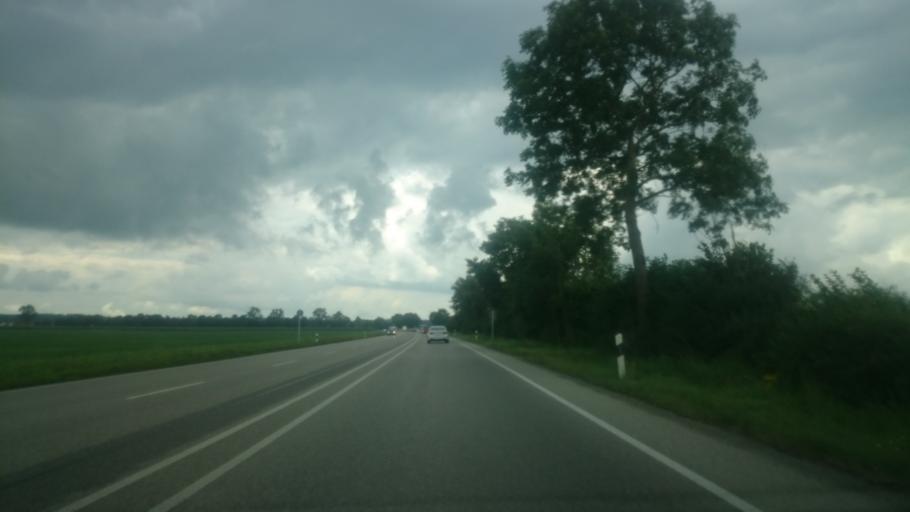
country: DE
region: Bavaria
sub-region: Swabia
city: Rieden
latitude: 47.9366
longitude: 10.6631
